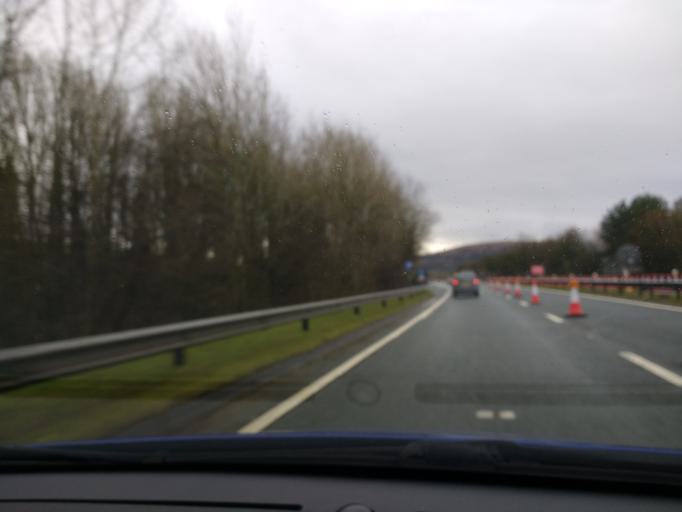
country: GB
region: England
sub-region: Cumbria
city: Milnthorpe
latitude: 54.2421
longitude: -2.7289
